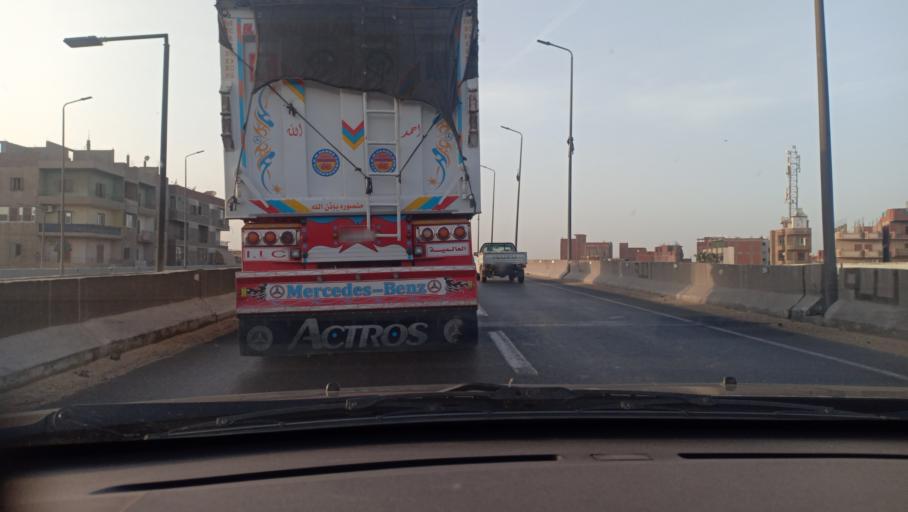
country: EG
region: Muhafazat al Minufiyah
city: Quwaysina
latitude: 30.5477
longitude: 31.2691
